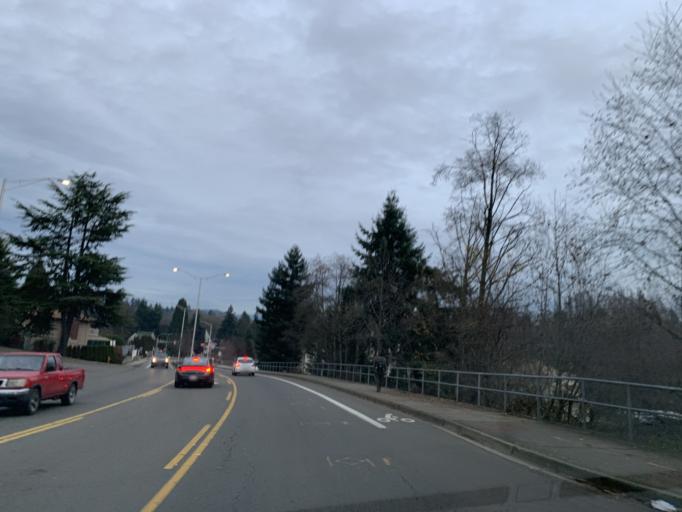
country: US
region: Washington
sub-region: King County
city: SeaTac
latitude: 47.4651
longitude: -122.2838
